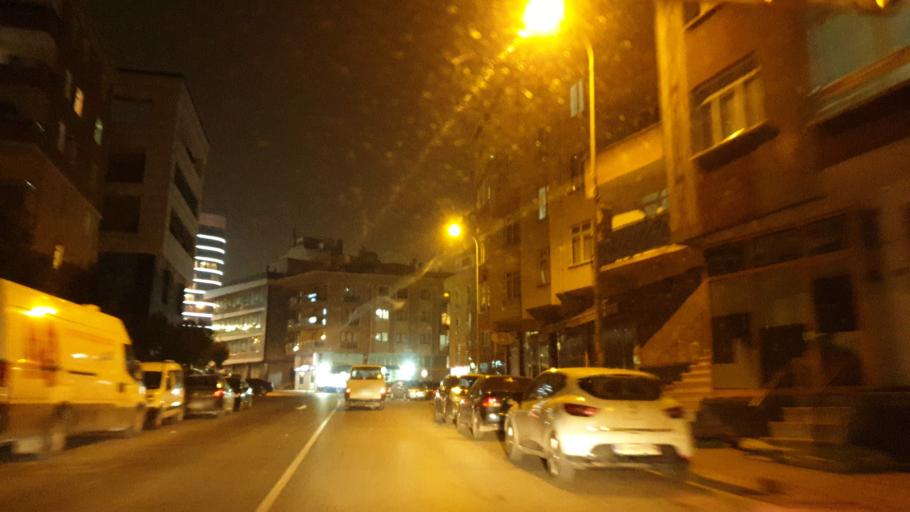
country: TR
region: Istanbul
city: Pendik
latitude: 40.8788
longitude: 29.2555
